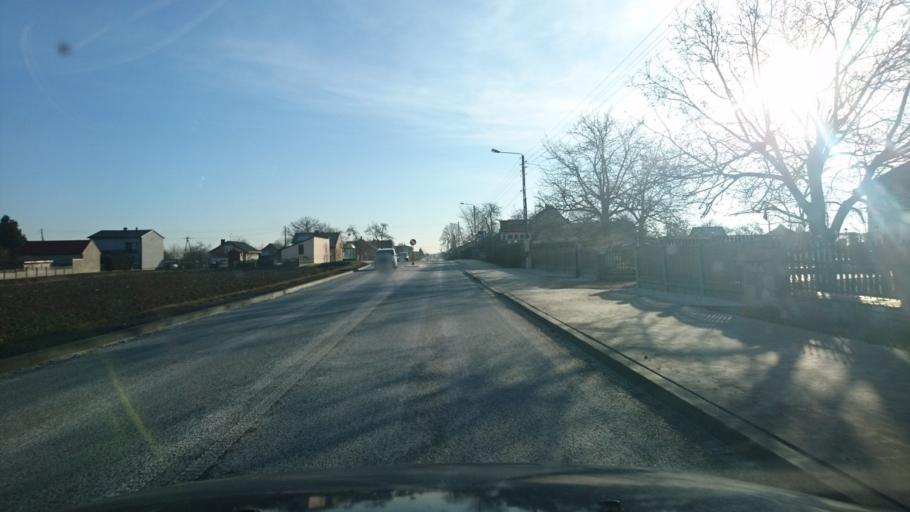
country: PL
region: Silesian Voivodeship
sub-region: Powiat klobucki
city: Starokrzepice
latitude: 51.0181
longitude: 18.6529
